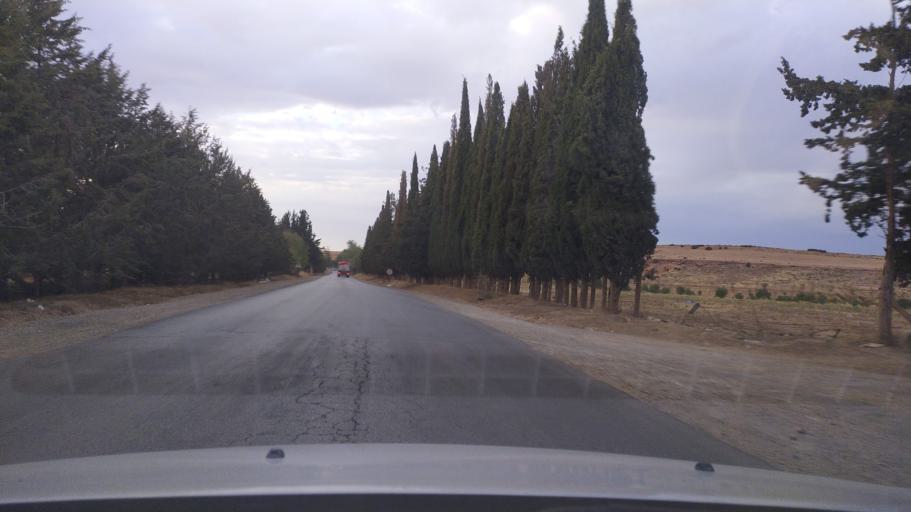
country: DZ
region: Tiaret
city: Frenda
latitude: 35.0455
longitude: 1.0847
